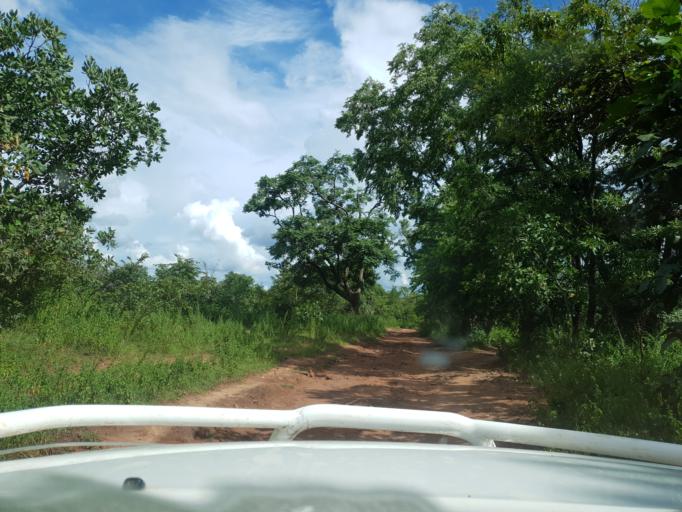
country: CI
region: Savanes
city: Tengrela
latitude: 10.4628
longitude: -6.7970
